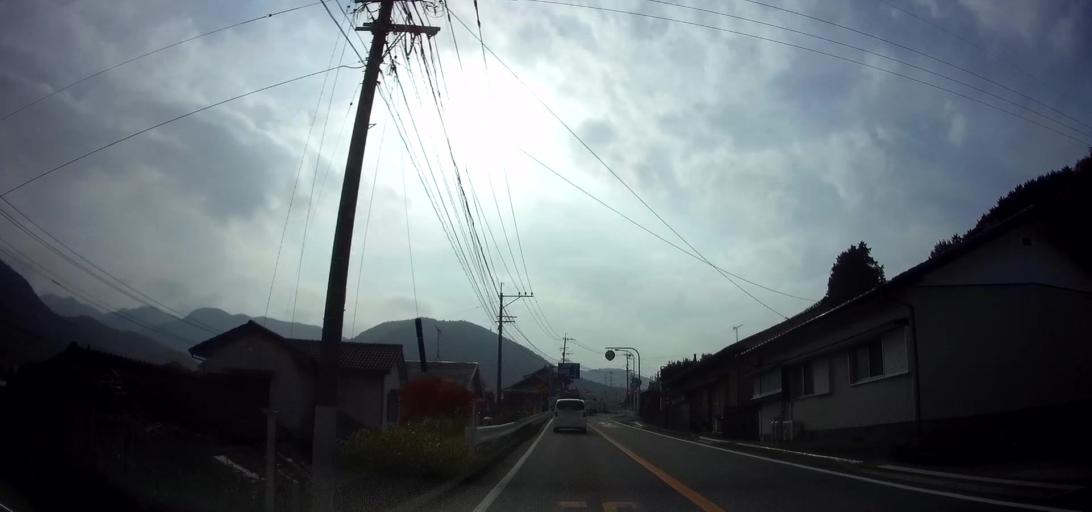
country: JP
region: Nagasaki
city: Shimabara
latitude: 32.7675
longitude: 130.2137
